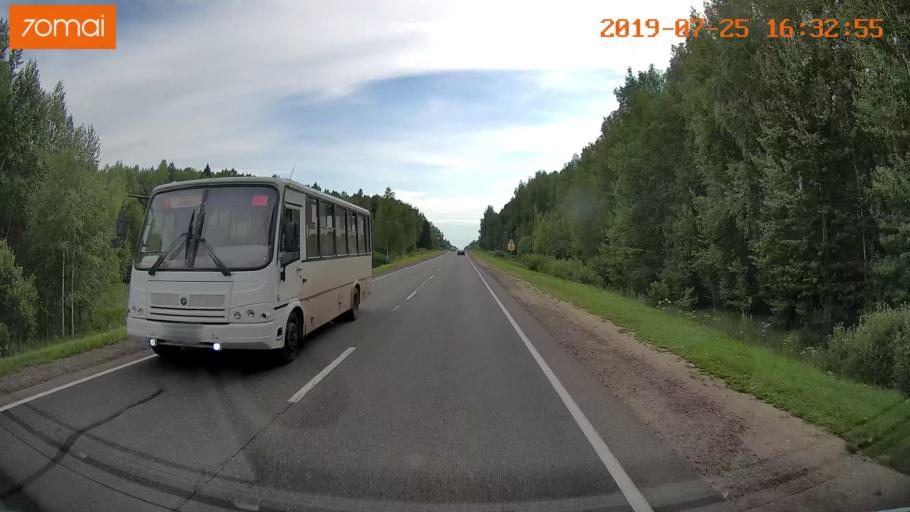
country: RU
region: Ivanovo
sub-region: Privolzhskiy Rayon
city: Ples
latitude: 57.4324
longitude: 41.4663
